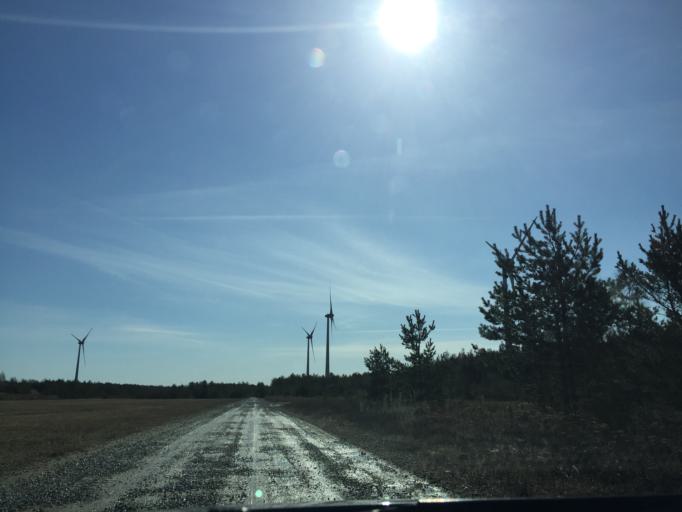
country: EE
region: Laeaene
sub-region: Lihula vald
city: Lihula
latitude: 58.6239
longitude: 23.5418
